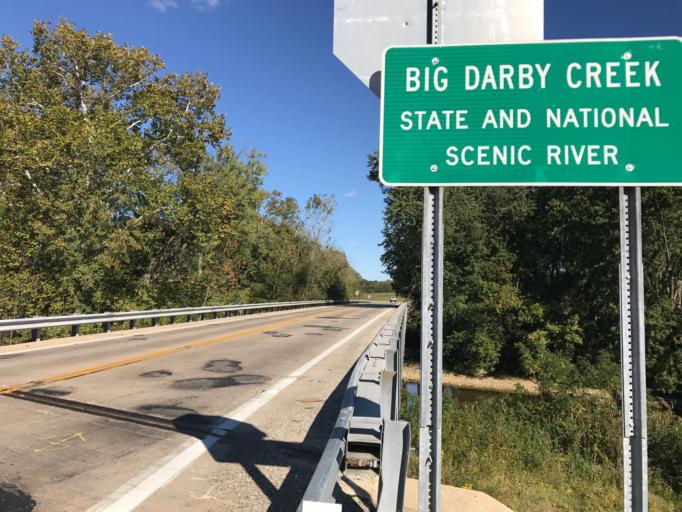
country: US
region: Ohio
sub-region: Franklin County
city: Grove City
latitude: 39.8024
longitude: -83.1699
